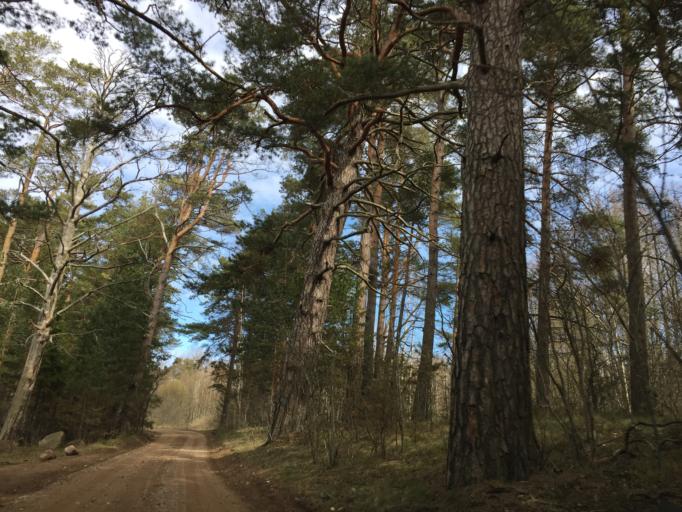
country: LV
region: Salacgrivas
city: Salacgriva
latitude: 57.5986
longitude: 24.3738
